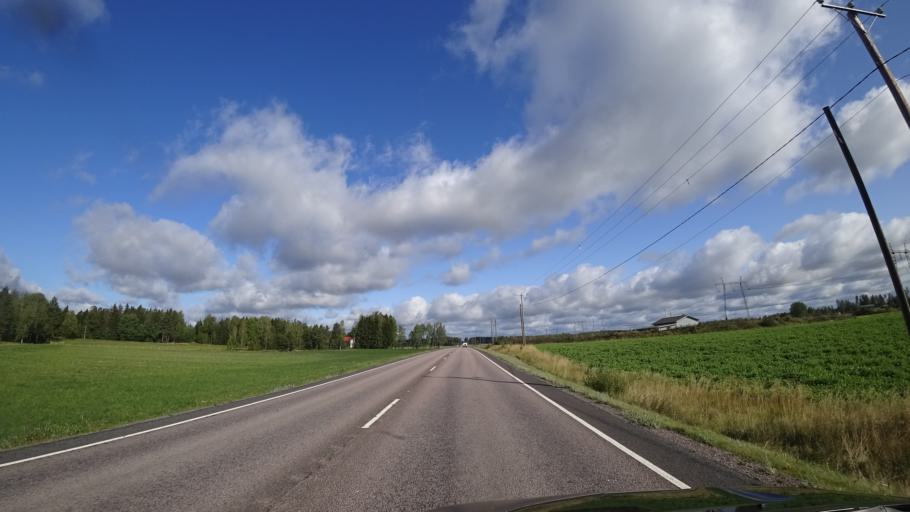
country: FI
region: Uusimaa
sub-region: Helsinki
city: Nurmijaervi
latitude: 60.5135
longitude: 24.9273
